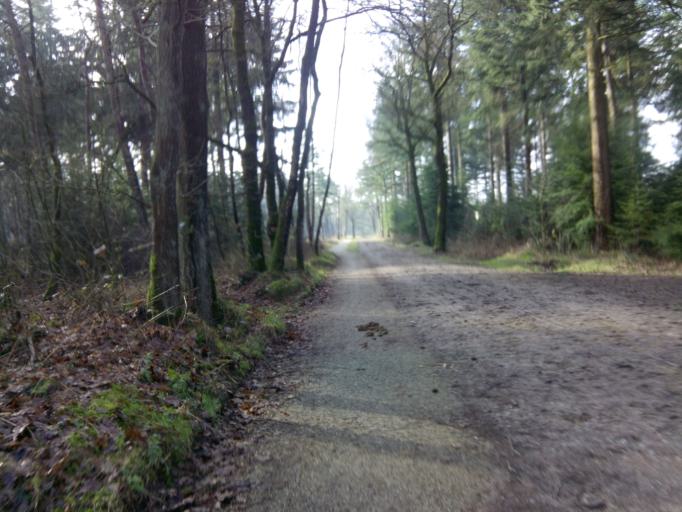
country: NL
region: Utrecht
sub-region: Gemeente Utrechtse Heuvelrug
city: Leersum
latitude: 52.0399
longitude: 5.4459
